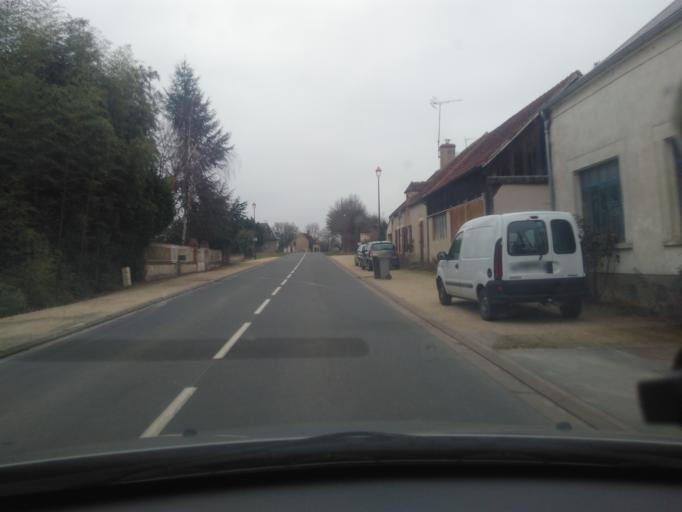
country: FR
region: Centre
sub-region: Departement du Cher
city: Le Chatelet
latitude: 46.6526
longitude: 2.3823
